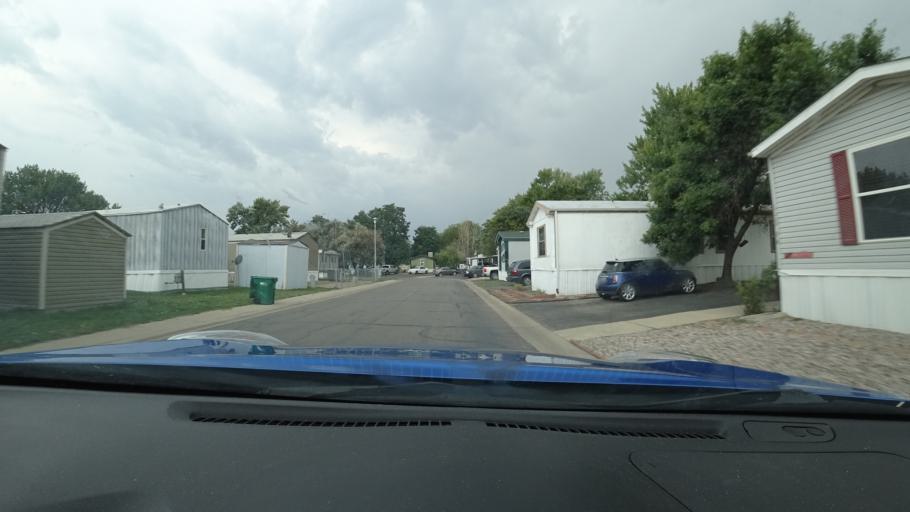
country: US
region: Colorado
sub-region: Adams County
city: Aurora
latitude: 39.7411
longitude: -104.7851
